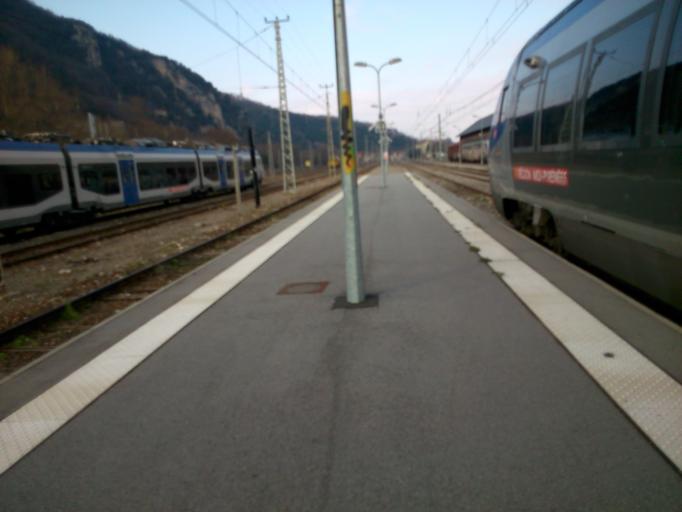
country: FR
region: Midi-Pyrenees
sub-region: Departement de l'Ariege
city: Foix
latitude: 42.9702
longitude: 1.6068
